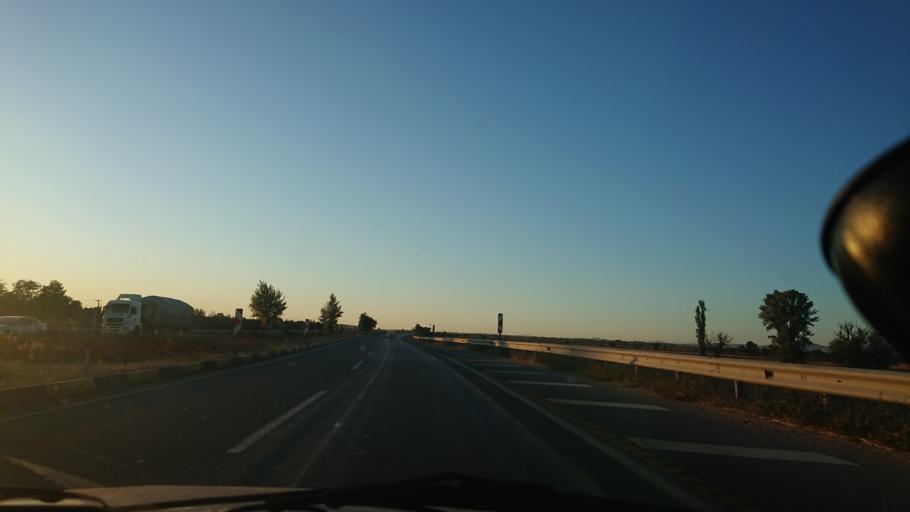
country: TR
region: Eskisehir
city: Mahmudiye
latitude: 39.5392
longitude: 30.9418
